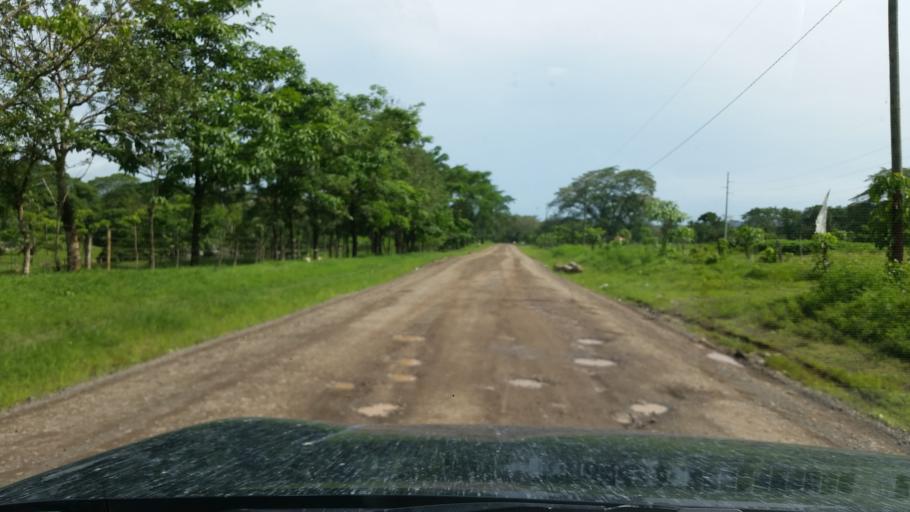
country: NI
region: Atlantico Norte (RAAN)
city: Siuna
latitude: 13.7096
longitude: -84.7761
